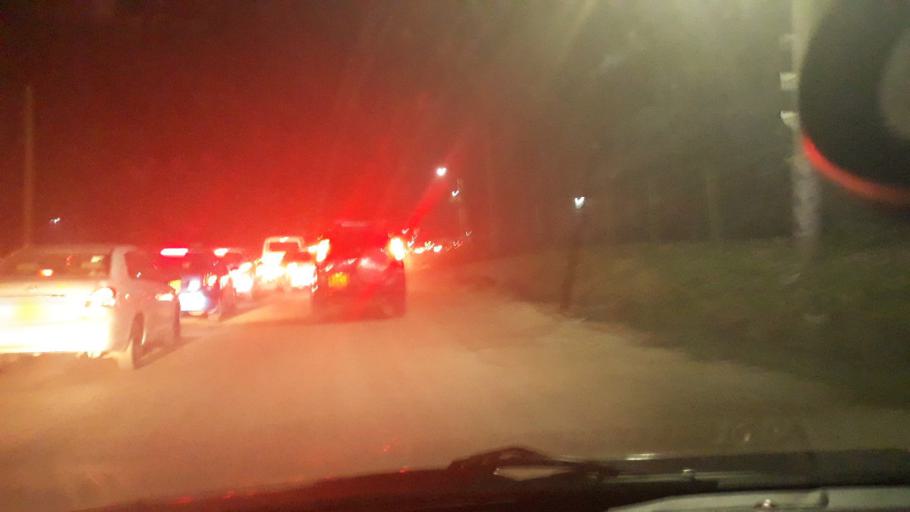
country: KE
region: Nairobi Area
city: Pumwani
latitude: -1.2767
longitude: 36.8857
